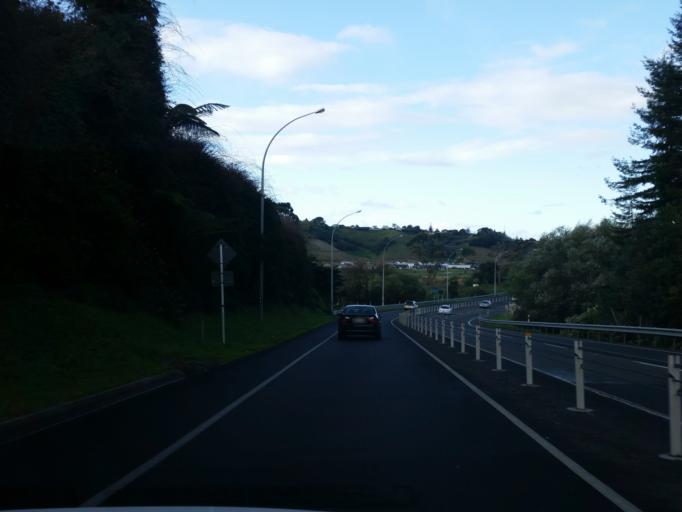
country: NZ
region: Bay of Plenty
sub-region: Tauranga City
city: Tauranga
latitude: -37.6947
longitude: 176.1183
